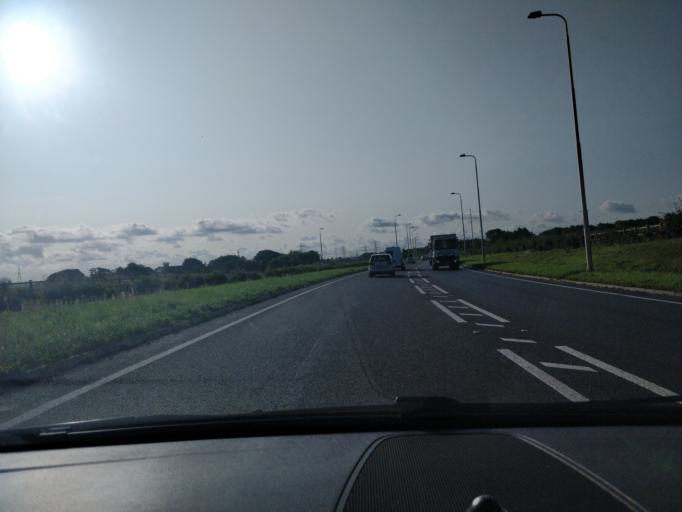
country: GB
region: England
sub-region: Sefton
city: Maghull
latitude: 53.4972
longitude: -2.9657
